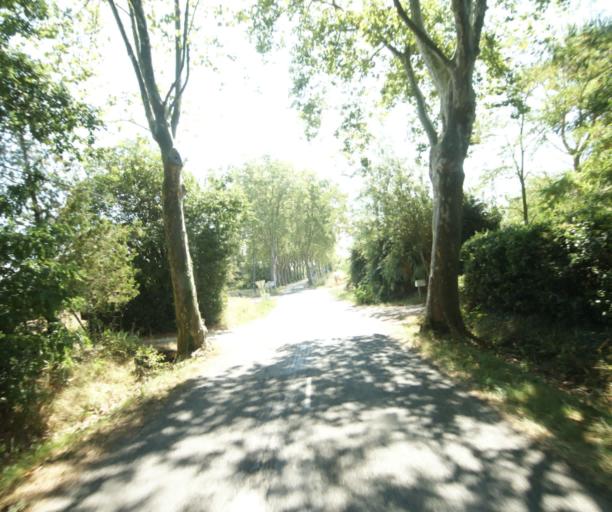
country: FR
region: Midi-Pyrenees
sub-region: Departement de la Haute-Garonne
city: Revel
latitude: 43.5031
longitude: 1.9499
